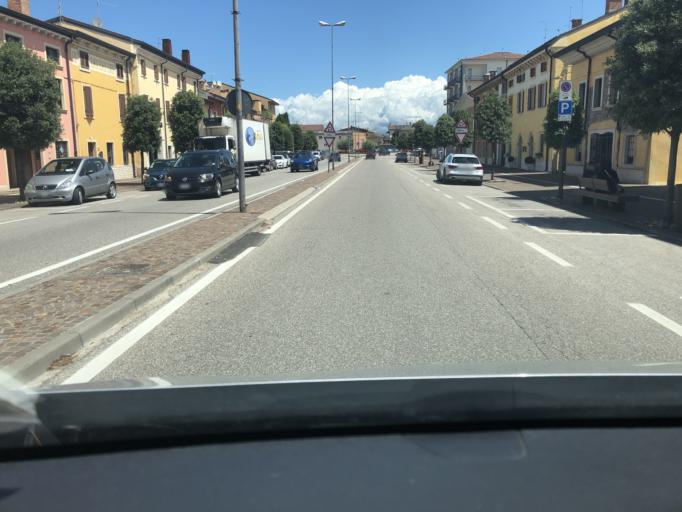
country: IT
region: Veneto
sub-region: Provincia di Verona
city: Villafranca di Verona
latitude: 45.3551
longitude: 10.8434
